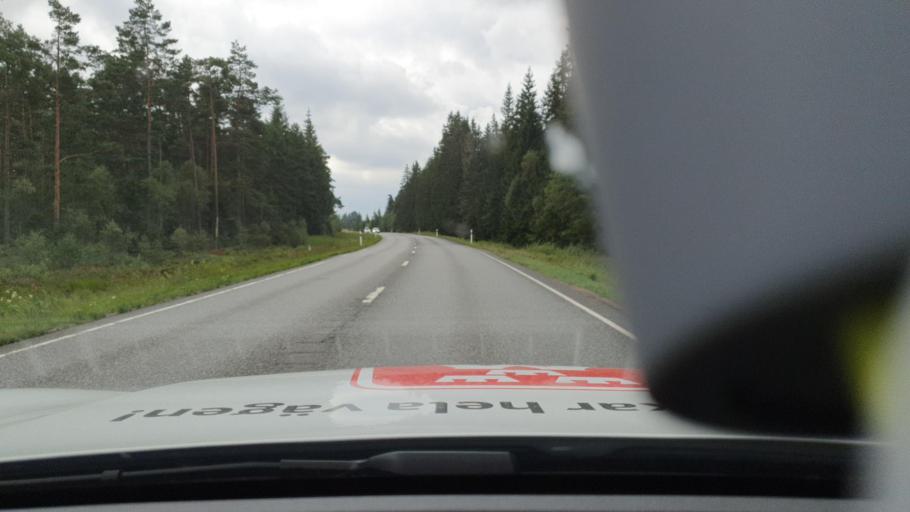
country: SE
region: Joenkoeping
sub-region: Gislaveds Kommun
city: Smalandsstenar
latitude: 57.2314
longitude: 13.4394
